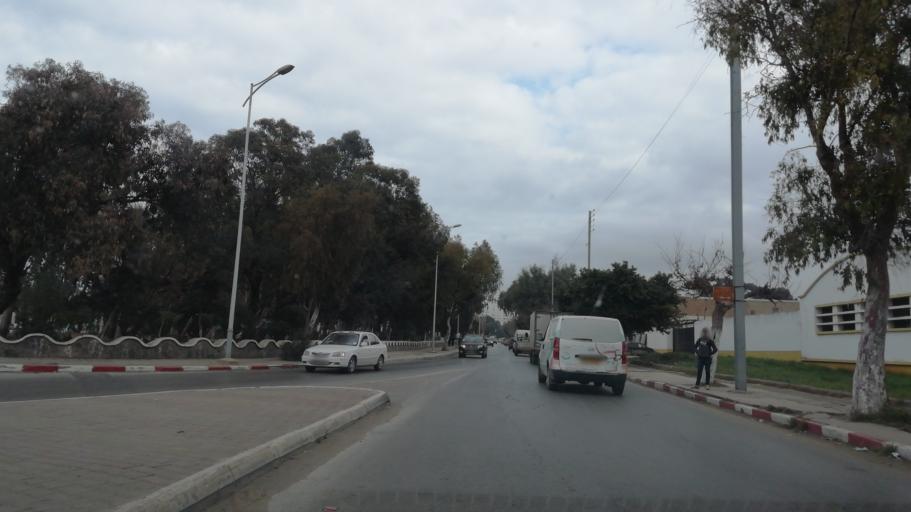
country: DZ
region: Oran
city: Oran
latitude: 35.6976
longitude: -0.6129
